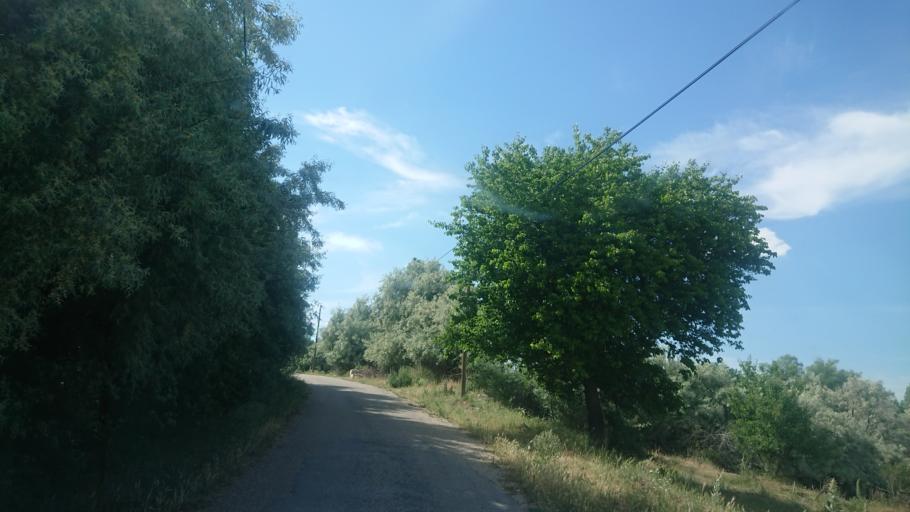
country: TR
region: Aksaray
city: Ortakoy
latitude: 38.8102
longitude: 33.9858
